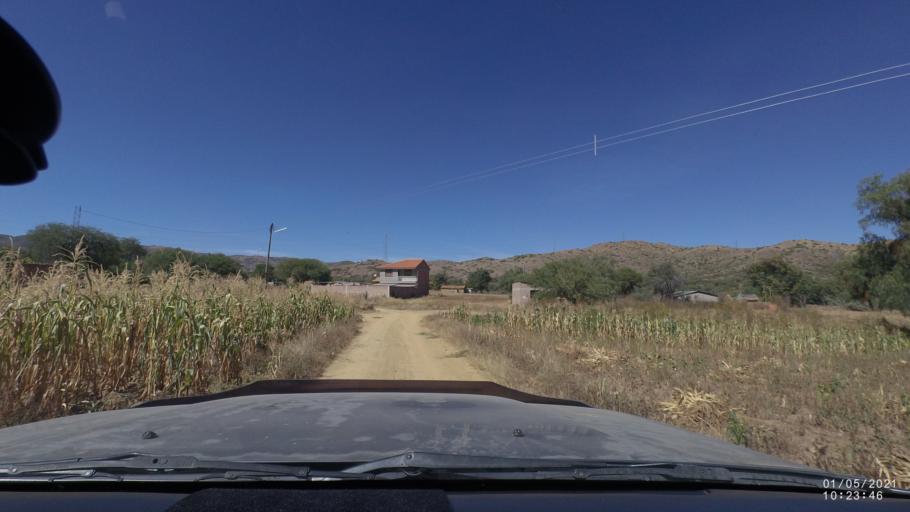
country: BO
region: Cochabamba
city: Capinota
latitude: -17.5730
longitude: -66.1959
